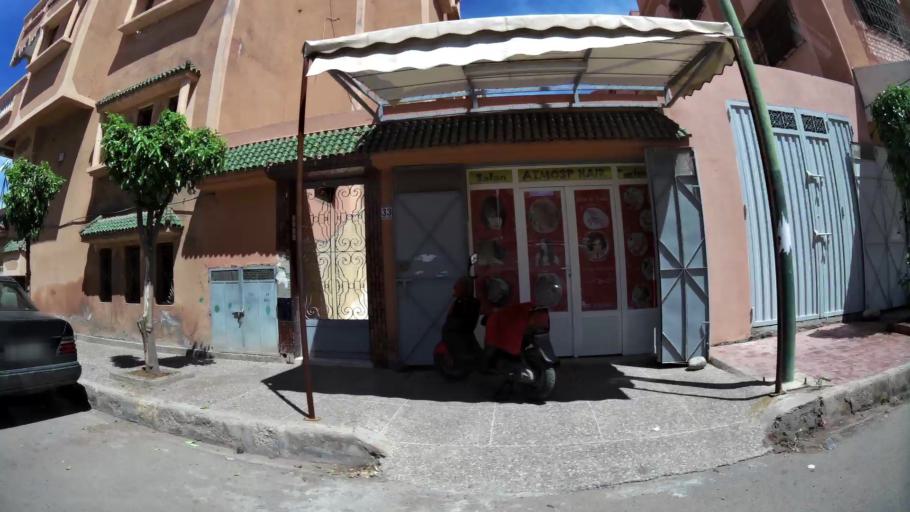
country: MA
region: Marrakech-Tensift-Al Haouz
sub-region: Marrakech
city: Marrakesh
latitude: 31.6468
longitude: -8.0671
